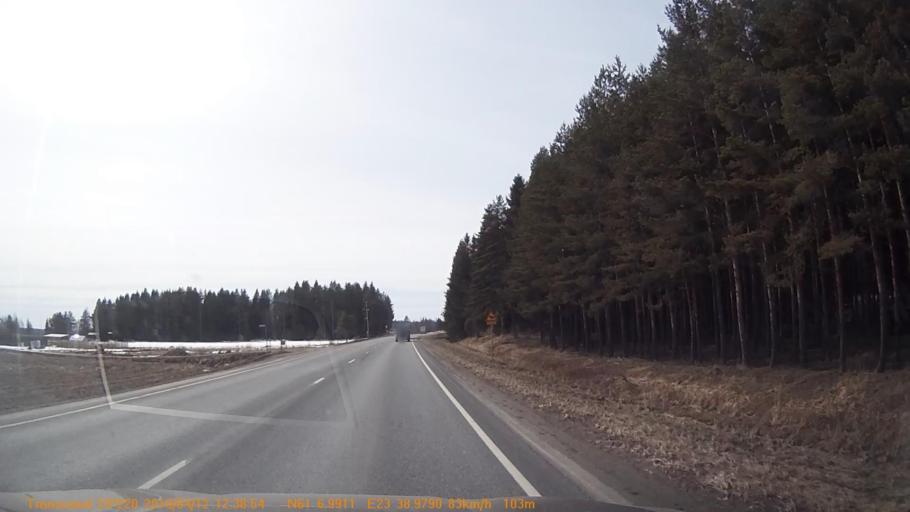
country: FI
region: Pirkanmaa
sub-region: Etelae-Pirkanmaa
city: Kylmaekoski
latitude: 61.1167
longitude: 23.6500
